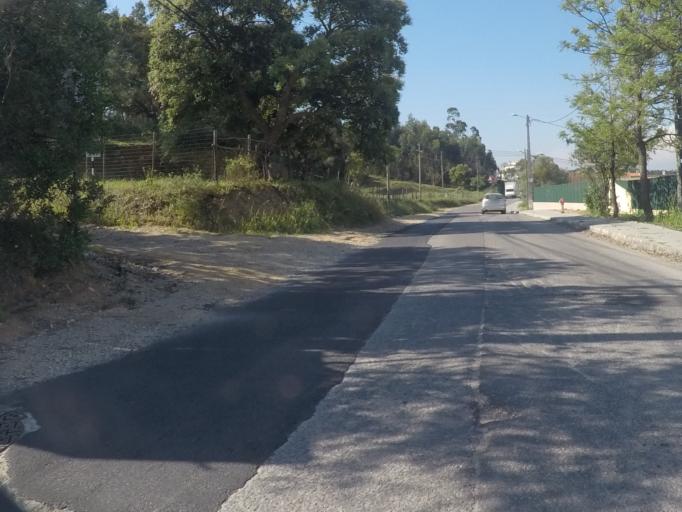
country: PT
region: Setubal
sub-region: Seixal
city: Amora
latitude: 38.6101
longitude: -9.1197
